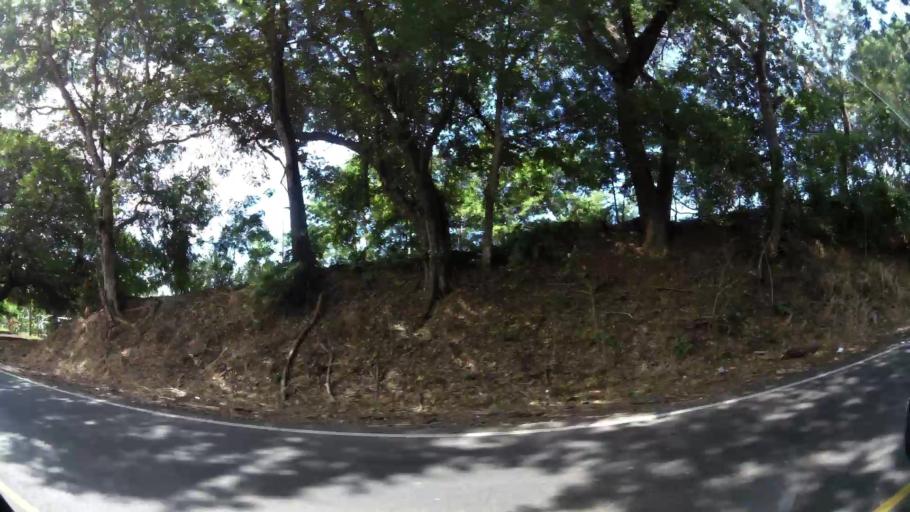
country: CR
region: Guanacaste
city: Juntas
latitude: 10.3155
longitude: -85.0444
